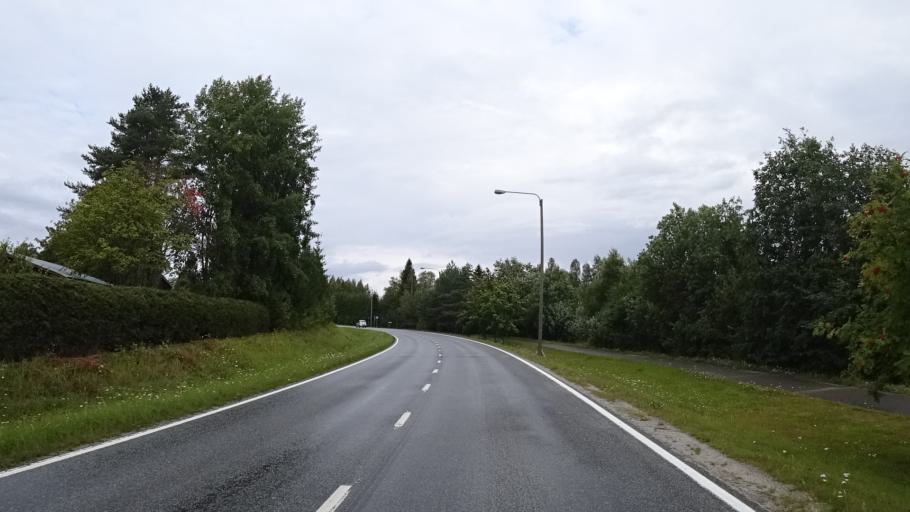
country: FI
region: Southern Savonia
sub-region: Savonlinna
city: Kerimaeki
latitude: 61.9215
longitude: 29.2819
